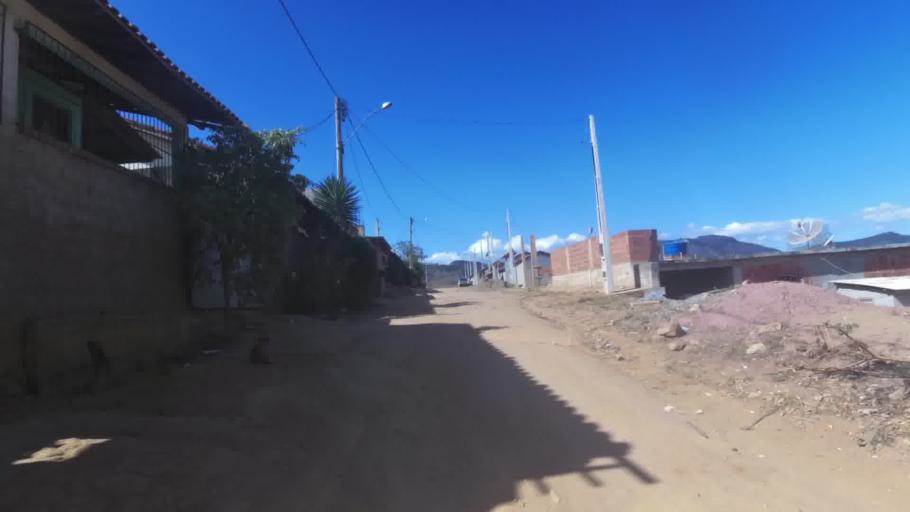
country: BR
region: Espirito Santo
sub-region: Cachoeiro De Itapemirim
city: Cachoeiro de Itapemirim
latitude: -20.9215
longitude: -41.1963
